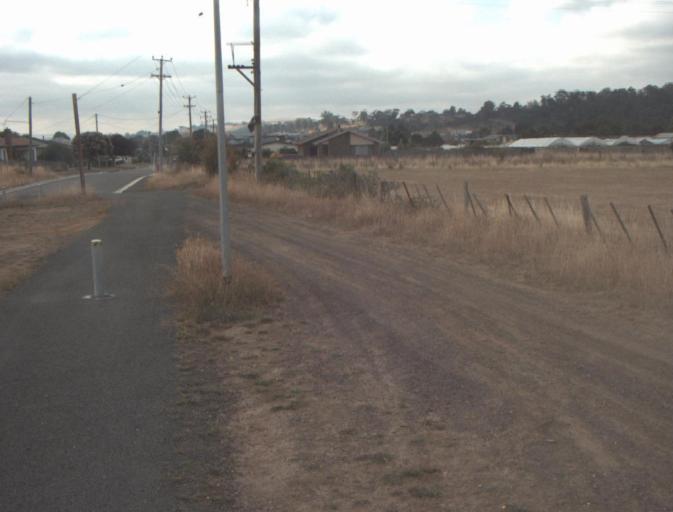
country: AU
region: Tasmania
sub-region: Launceston
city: Summerhill
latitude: -41.4820
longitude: 147.1577
